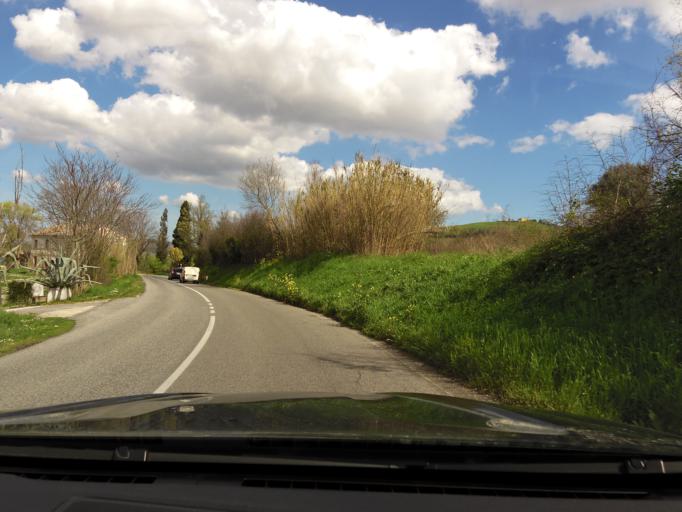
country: IT
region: The Marches
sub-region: Provincia di Ancona
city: Castelfidardo
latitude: 43.4762
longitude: 13.5558
